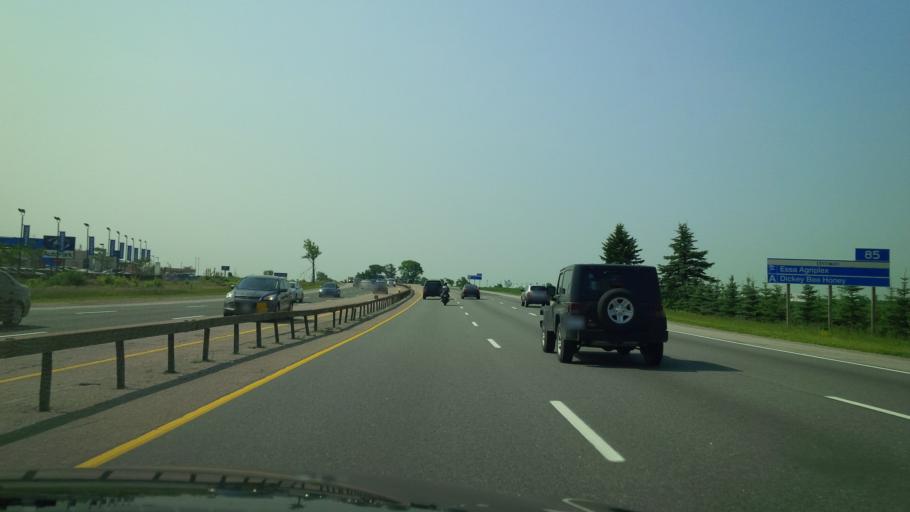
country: CA
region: Ontario
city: Innisfil
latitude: 44.3039
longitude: -79.6840
